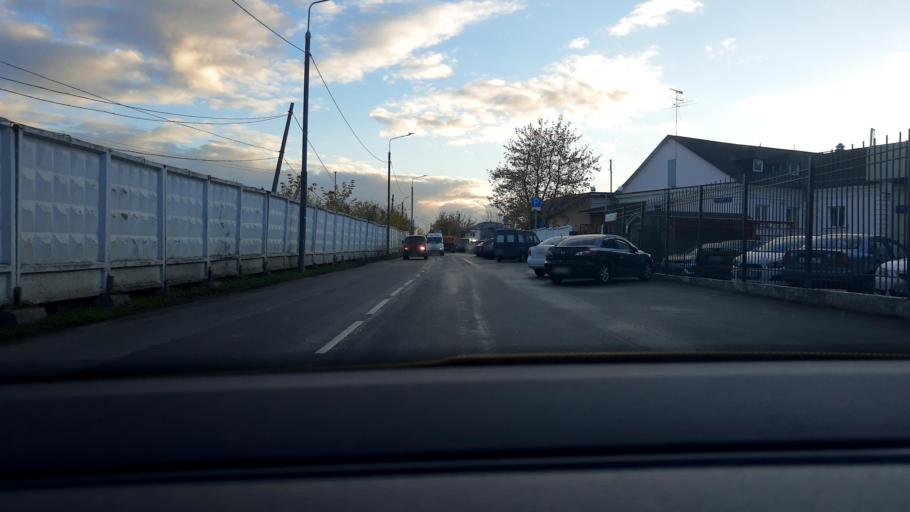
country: RU
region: Moscow
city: Strogino
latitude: 55.7885
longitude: 37.3988
